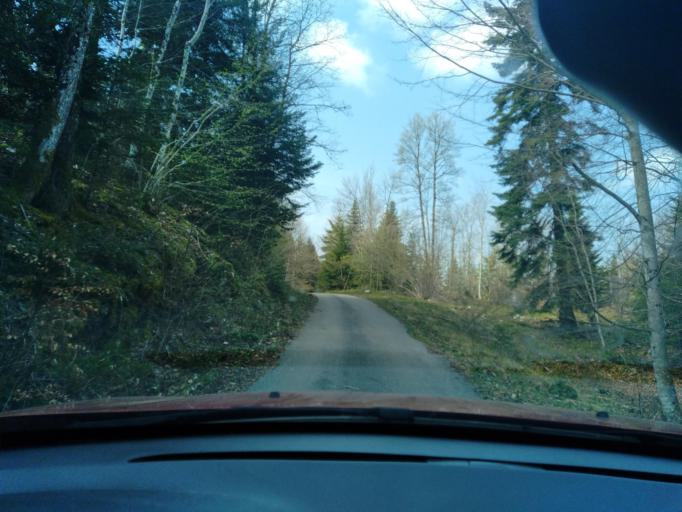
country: FR
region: Franche-Comte
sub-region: Departement du Jura
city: Moirans-en-Montagne
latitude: 46.4731
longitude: 5.7625
